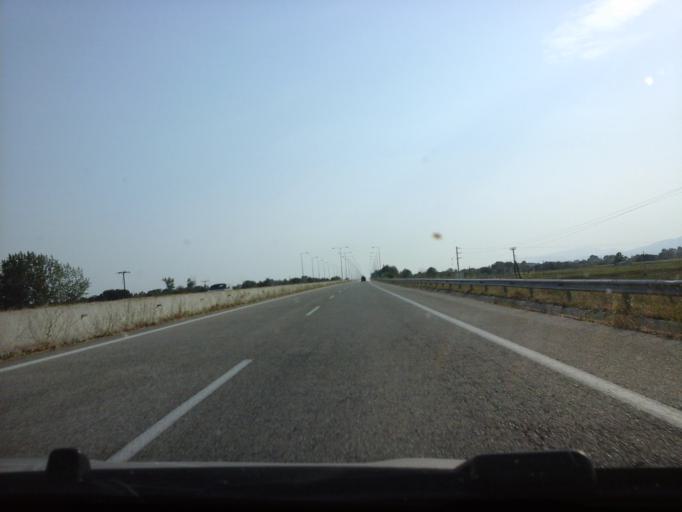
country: GR
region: East Macedonia and Thrace
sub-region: Nomos Xanthis
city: Genissea
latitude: 41.1014
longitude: 24.9547
